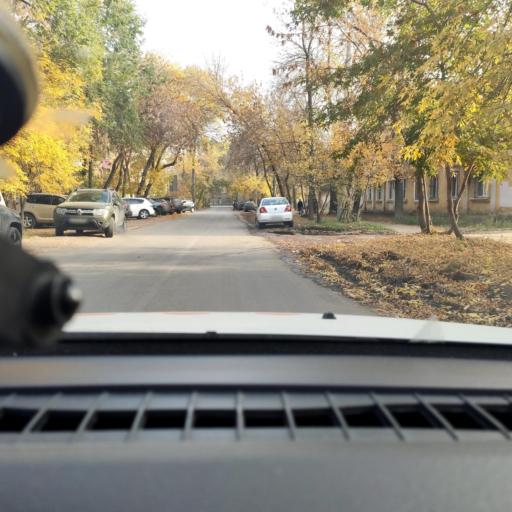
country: RU
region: Samara
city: Samara
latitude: 53.1180
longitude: 50.0790
